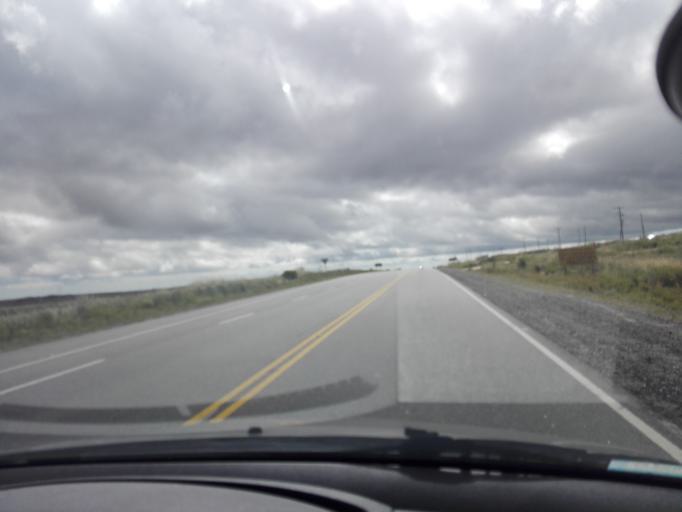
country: AR
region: Cordoba
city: Mina Clavero
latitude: -31.6177
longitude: -64.8706
